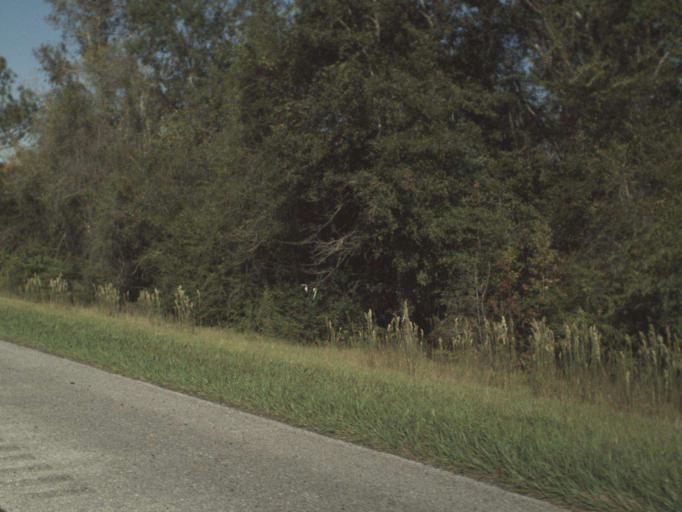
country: US
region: Florida
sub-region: Holmes County
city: Bonifay
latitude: 30.7610
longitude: -85.7494
